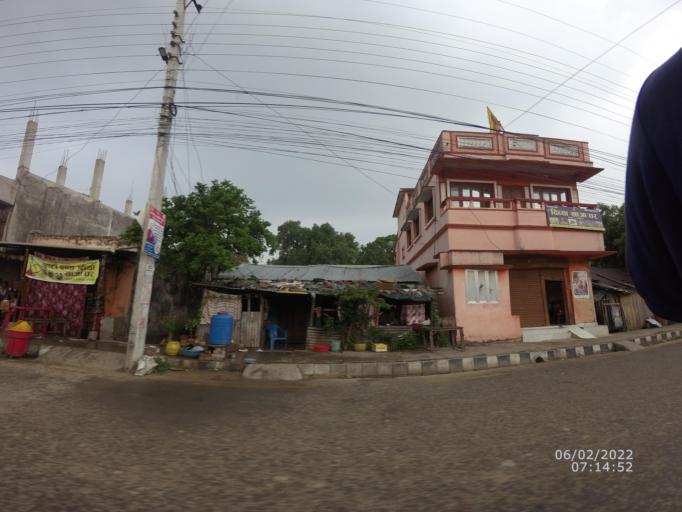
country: NP
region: Western Region
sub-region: Lumbini Zone
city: Bhairahawa
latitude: 27.4807
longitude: 83.4431
